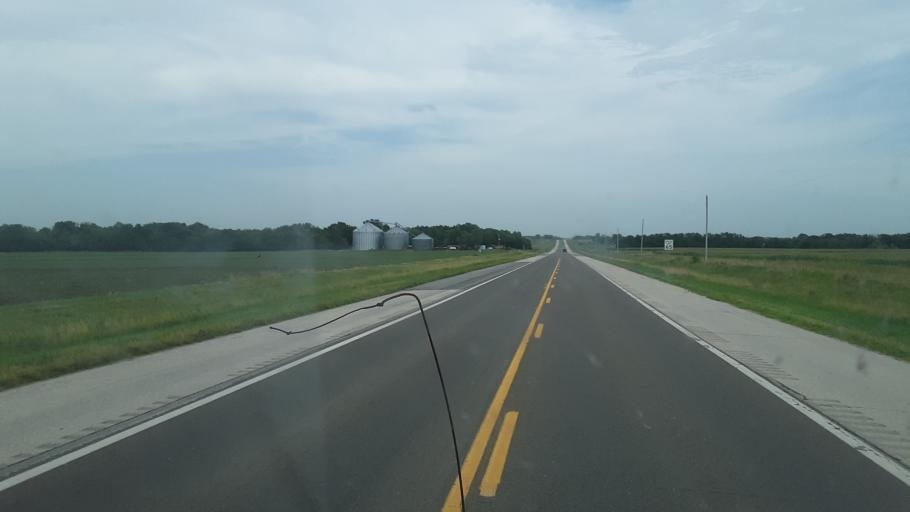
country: US
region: Kansas
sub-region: Allen County
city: Iola
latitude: 37.9222
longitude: -95.4805
